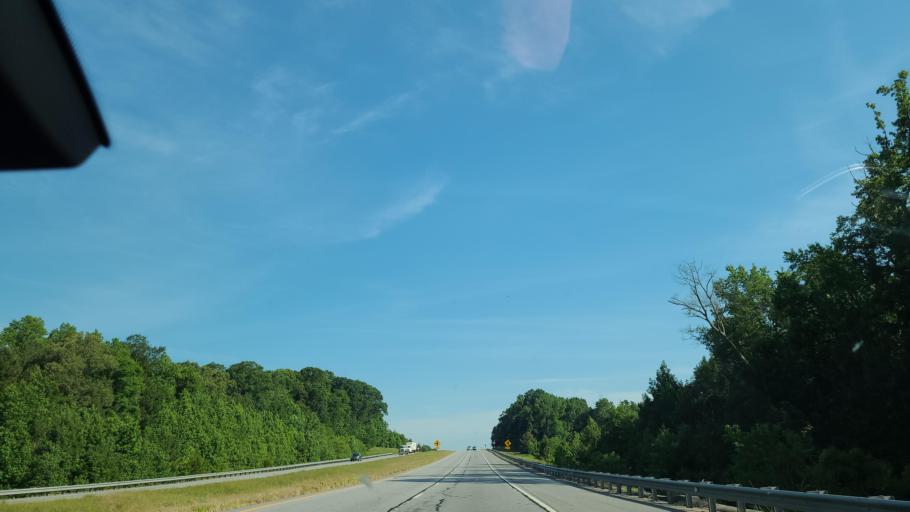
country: US
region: Georgia
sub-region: Jackson County
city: Nicholson
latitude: 34.0909
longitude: -83.4273
